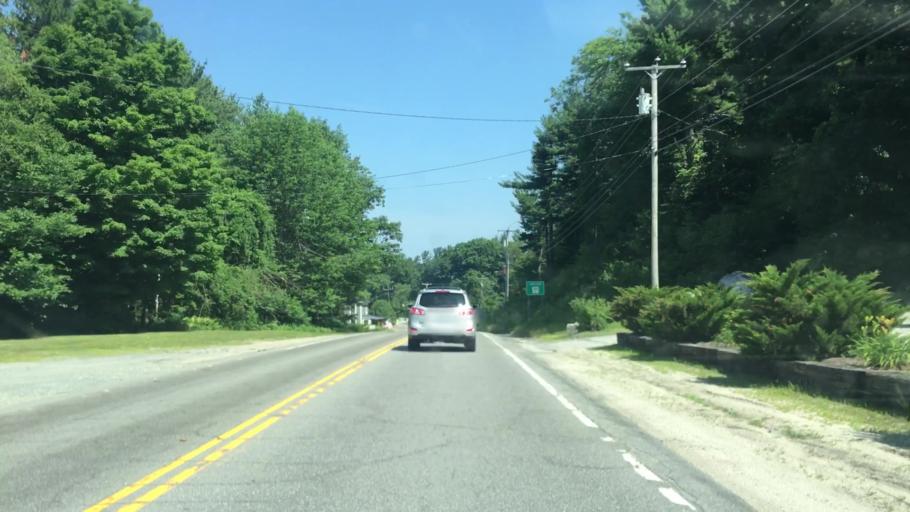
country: US
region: New Hampshire
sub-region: Merrimack County
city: Newbury
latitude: 43.3178
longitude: -72.0337
